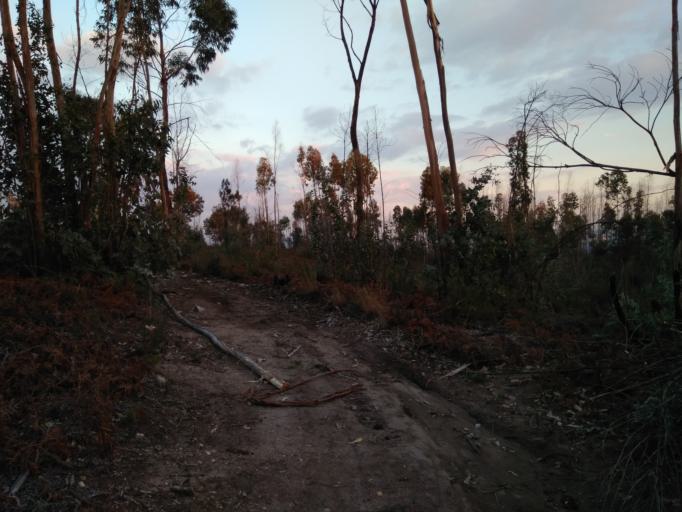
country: PT
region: Porto
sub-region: Vila Nova de Gaia
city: Vilar de Andorinho
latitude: 41.1027
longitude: -8.5848
